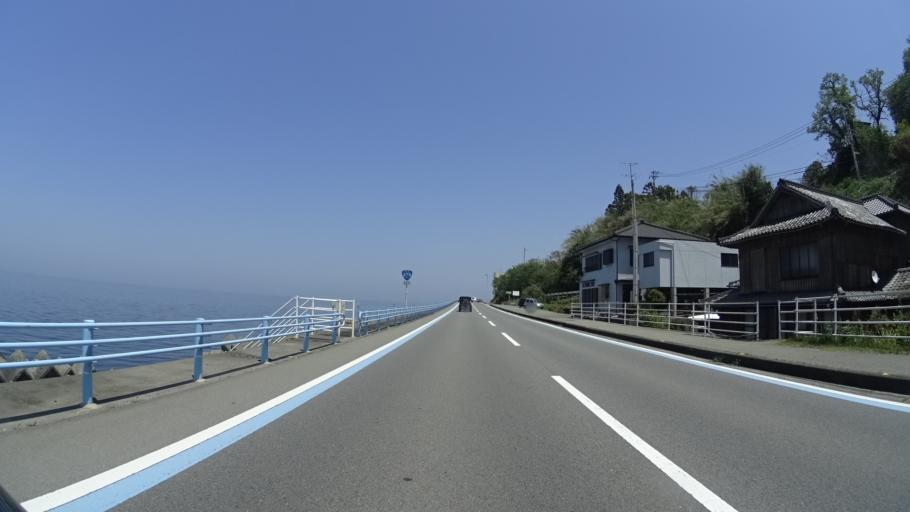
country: JP
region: Ehime
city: Iyo
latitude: 33.6710
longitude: 132.6108
